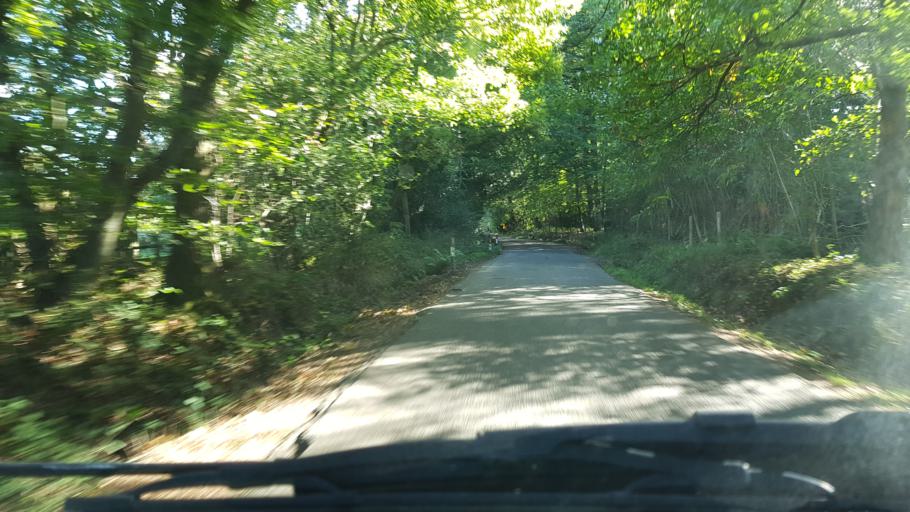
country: GB
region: England
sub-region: Surrey
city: Chiddingfold
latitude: 51.0881
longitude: -0.5857
